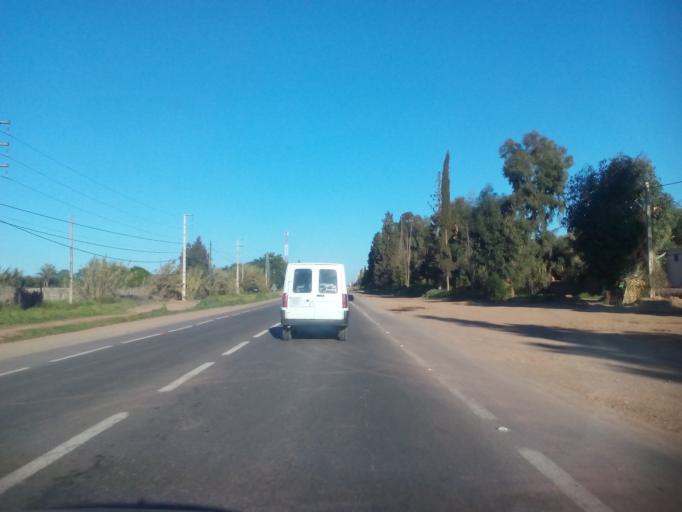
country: MA
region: Marrakech-Tensift-Al Haouz
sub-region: Marrakech
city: Marrakesh
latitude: 31.6315
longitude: -8.1839
